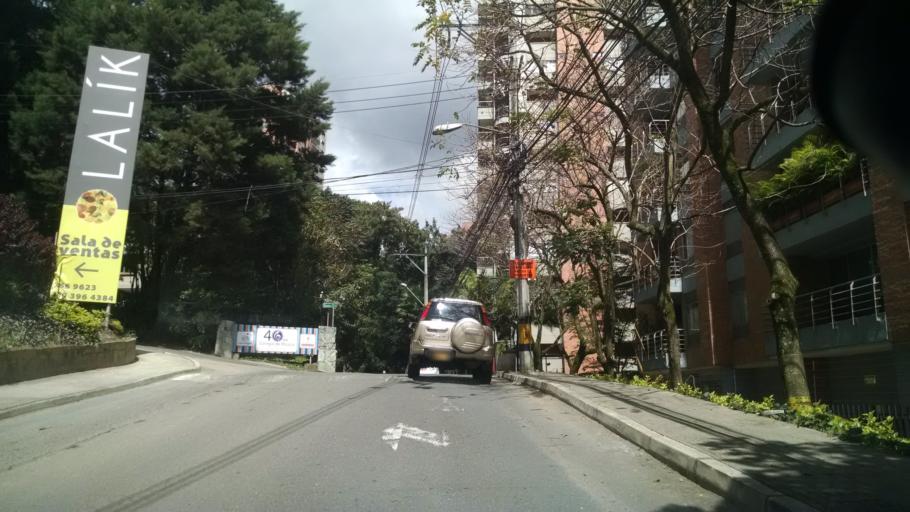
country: CO
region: Antioquia
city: Medellin
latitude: 6.2119
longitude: -75.5665
